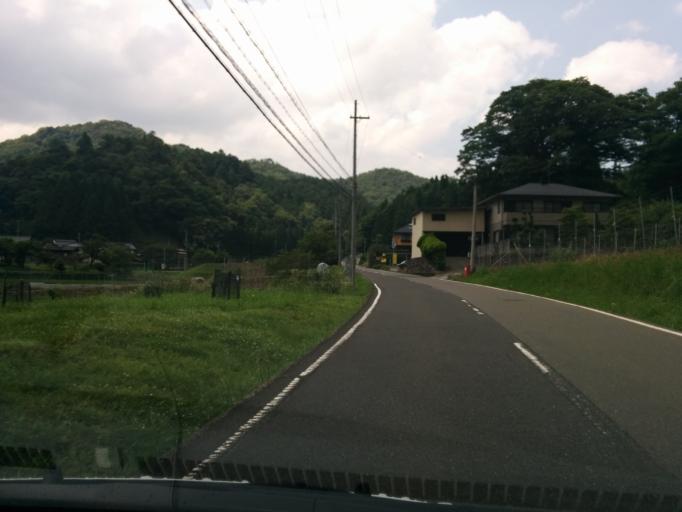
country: JP
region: Kyoto
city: Miyazu
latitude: 35.4258
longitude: 135.1575
